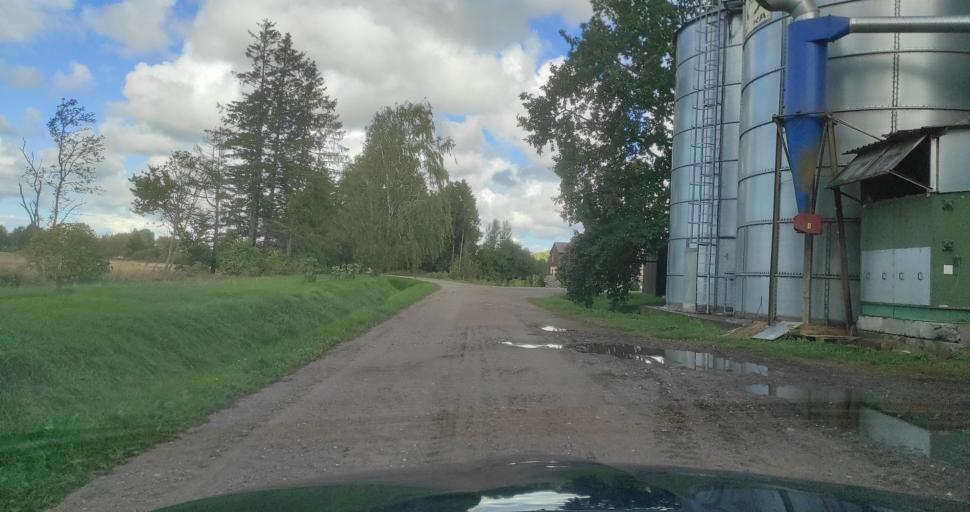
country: LV
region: Ventspils Rajons
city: Piltene
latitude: 57.2683
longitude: 21.5885
